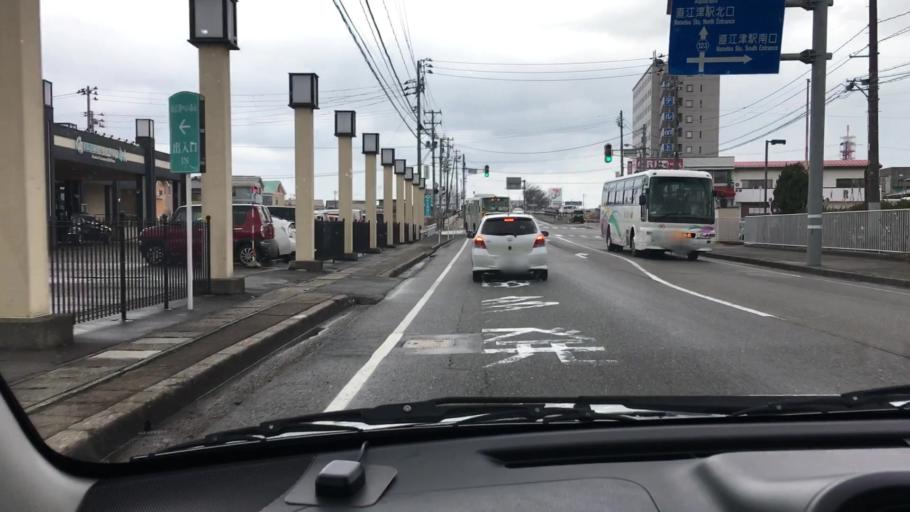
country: JP
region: Niigata
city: Joetsu
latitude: 37.1647
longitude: 138.2372
